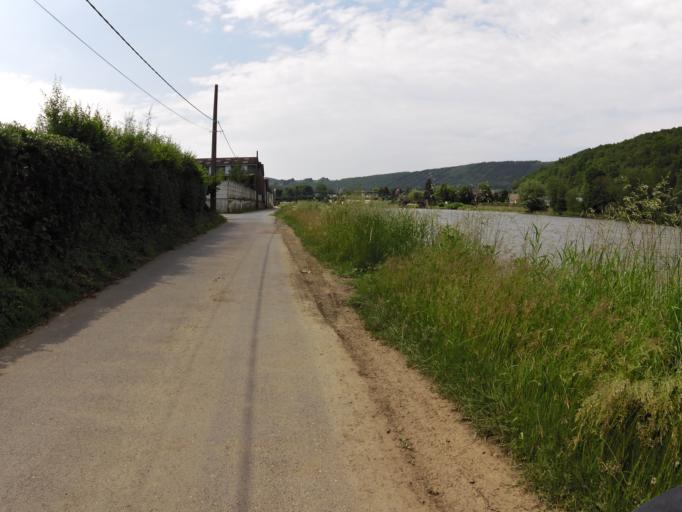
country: FR
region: Champagne-Ardenne
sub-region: Departement des Ardennes
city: Thilay
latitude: 49.8510
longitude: 4.7719
